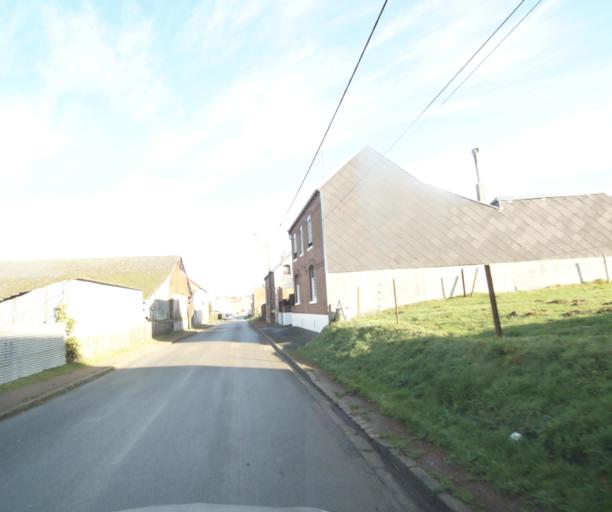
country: FR
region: Nord-Pas-de-Calais
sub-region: Departement du Nord
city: Maing
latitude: 50.3047
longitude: 3.4844
